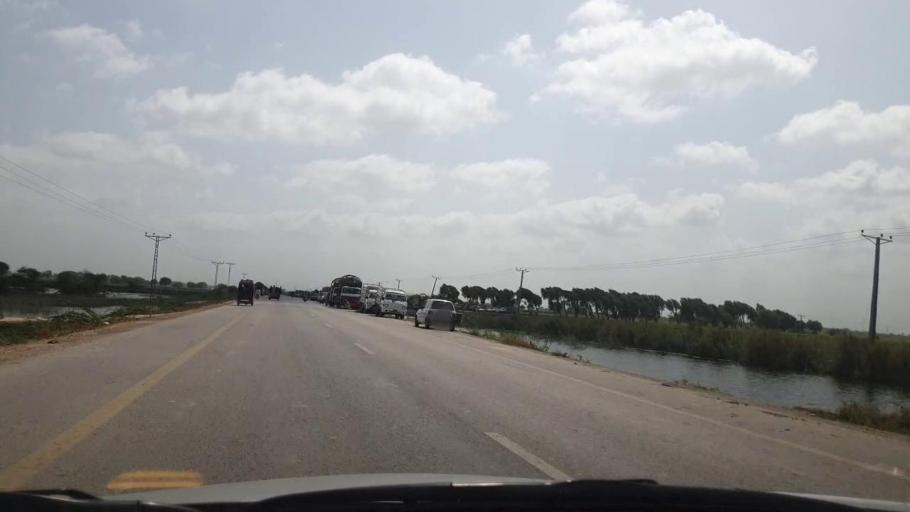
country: PK
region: Sindh
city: Talhar
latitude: 24.8952
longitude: 68.7857
